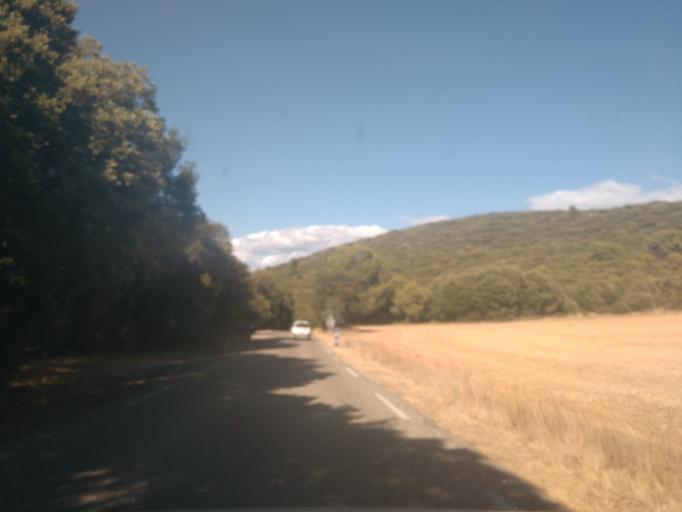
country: FR
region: Provence-Alpes-Cote d'Azur
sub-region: Departement du Var
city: Regusse
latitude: 43.7279
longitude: 6.1260
